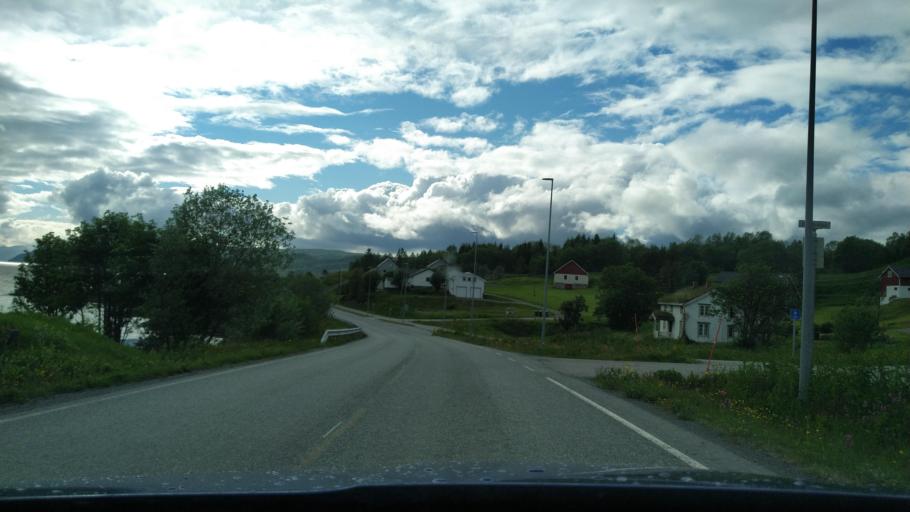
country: NO
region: Troms
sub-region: Sorreisa
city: Sorreisa
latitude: 69.1786
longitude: 18.0694
